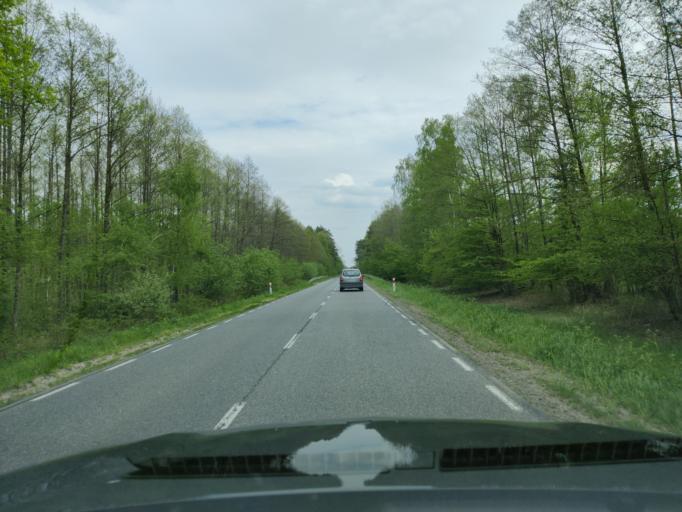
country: PL
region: Masovian Voivodeship
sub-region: Powiat pultuski
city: Obryte
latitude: 52.6375
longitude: 21.2885
